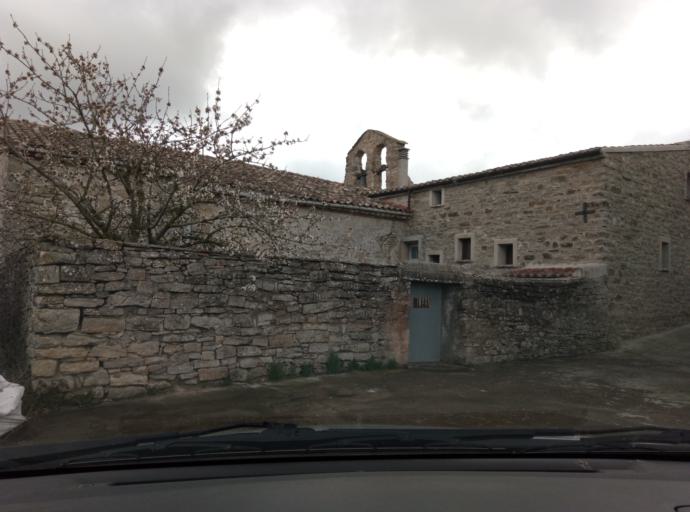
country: ES
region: Catalonia
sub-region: Provincia de Tarragona
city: Santa Coloma de Queralt
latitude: 41.5431
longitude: 1.3598
